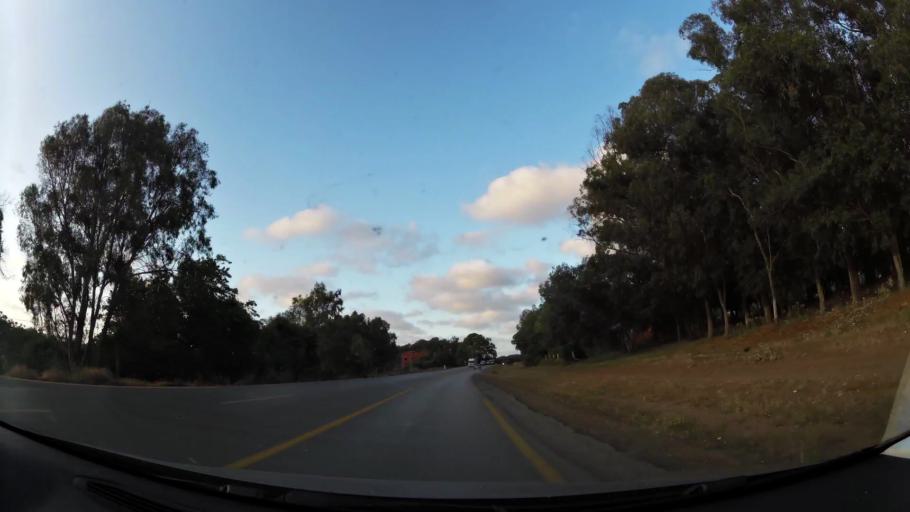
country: MA
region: Gharb-Chrarda-Beni Hssen
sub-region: Kenitra Province
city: Kenitra
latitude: 34.2215
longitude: -6.6613
